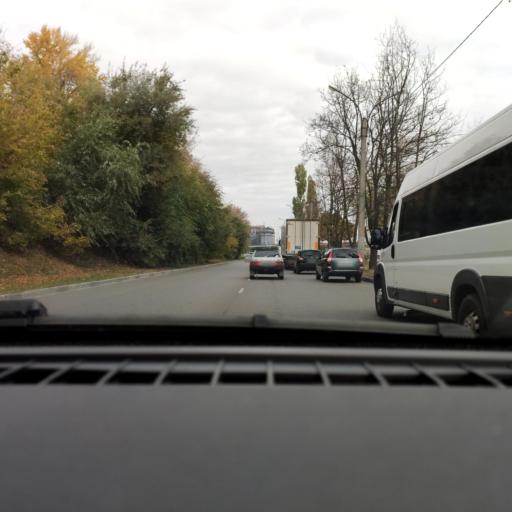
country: RU
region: Voronezj
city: Voronezh
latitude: 51.6645
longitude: 39.2200
